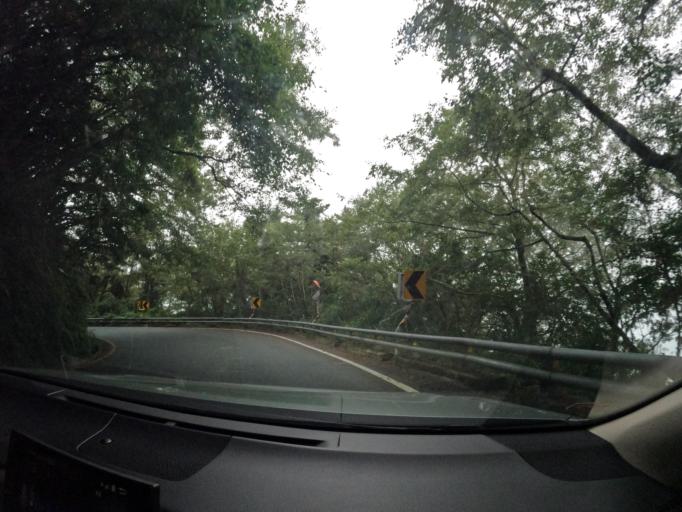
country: TW
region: Taiwan
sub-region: Taitung
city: Taitung
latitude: 23.2430
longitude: 120.9850
